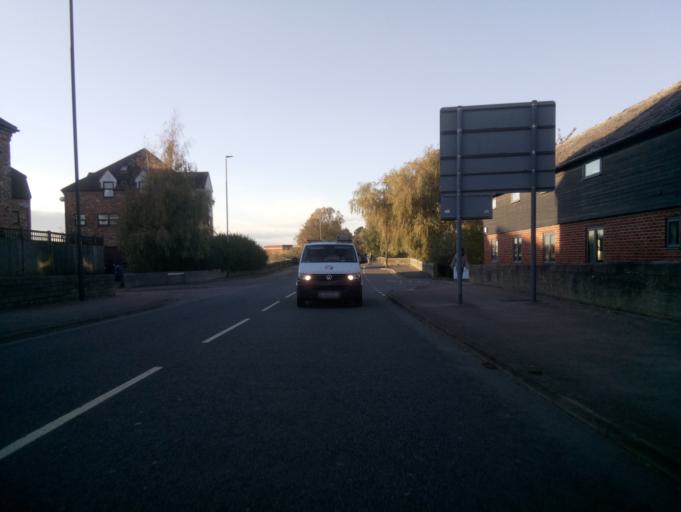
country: GB
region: England
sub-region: Gloucestershire
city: Tewkesbury
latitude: 51.9977
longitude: -2.1565
